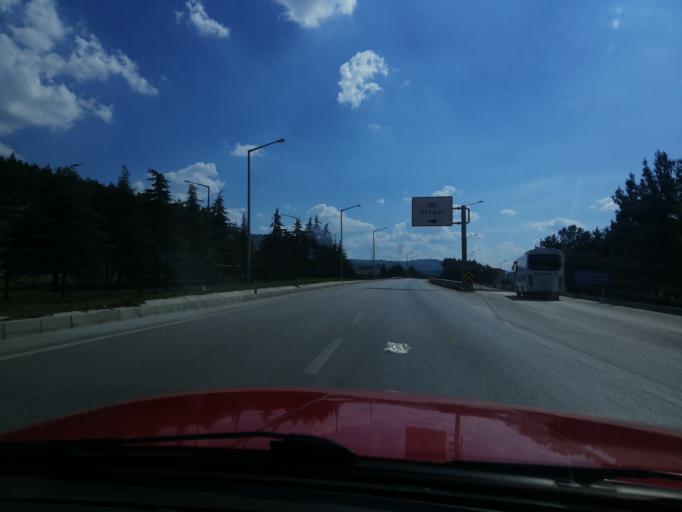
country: TR
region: Burdur
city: Burdur
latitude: 37.7388
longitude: 30.3118
